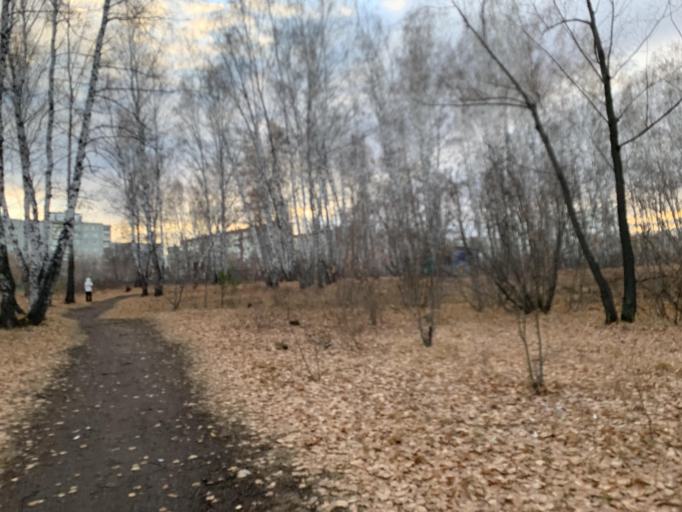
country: RU
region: Chelyabinsk
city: Roshchino
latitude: 55.2004
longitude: 61.3112
